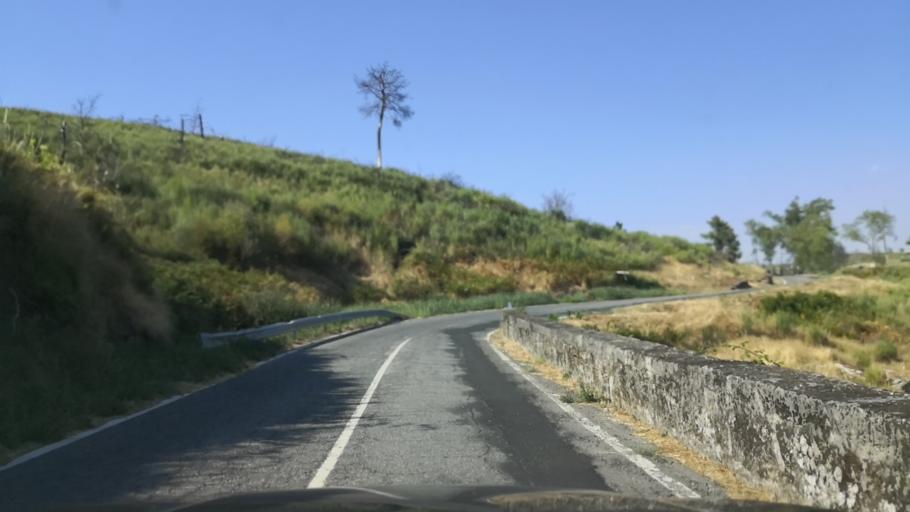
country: PT
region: Vila Real
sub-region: Murca
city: Murca
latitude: 41.3037
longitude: -7.4763
